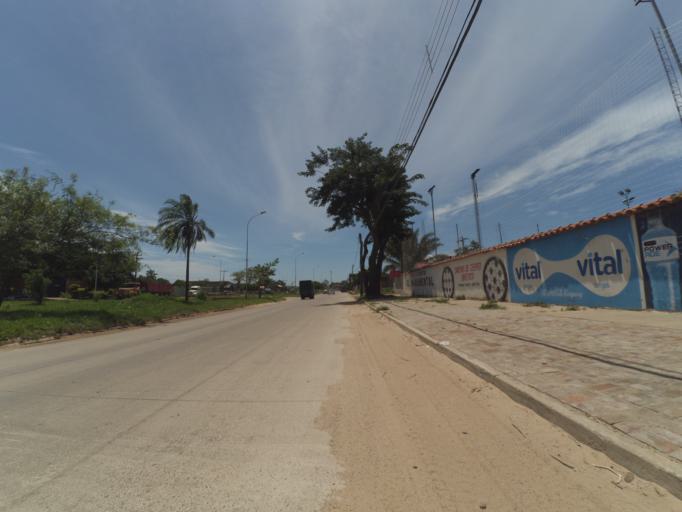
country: BO
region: Santa Cruz
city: Santa Cruz de la Sierra
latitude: -17.8110
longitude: -63.2219
